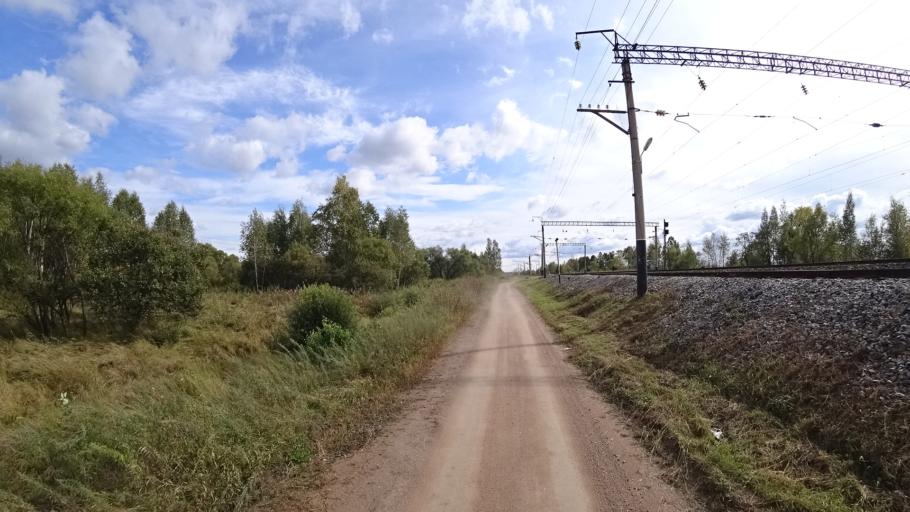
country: RU
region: Amur
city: Arkhara
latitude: 49.3450
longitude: 130.1645
